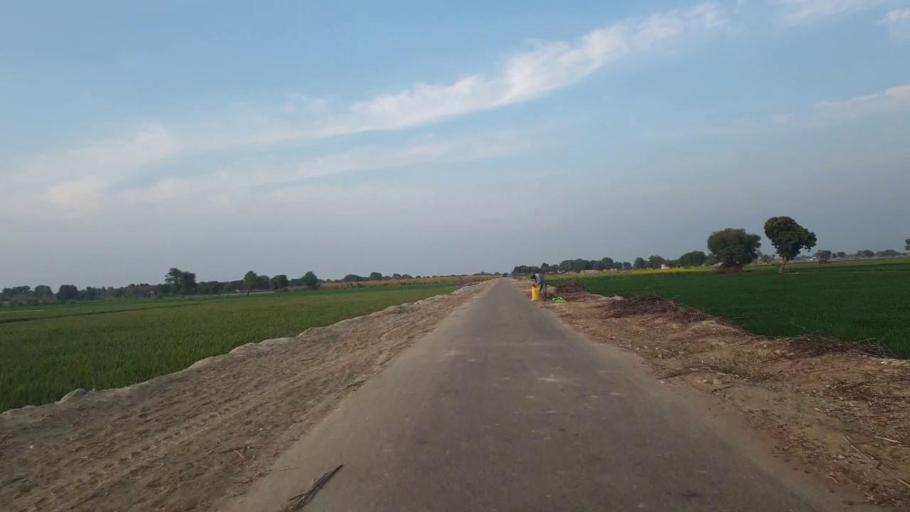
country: PK
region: Sindh
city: Shahpur Chakar
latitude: 26.1050
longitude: 68.5465
